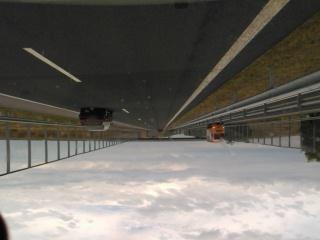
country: BG
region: Sliven
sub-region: Obshtina Sliven
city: Kermen
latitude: 42.5088
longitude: 26.3478
